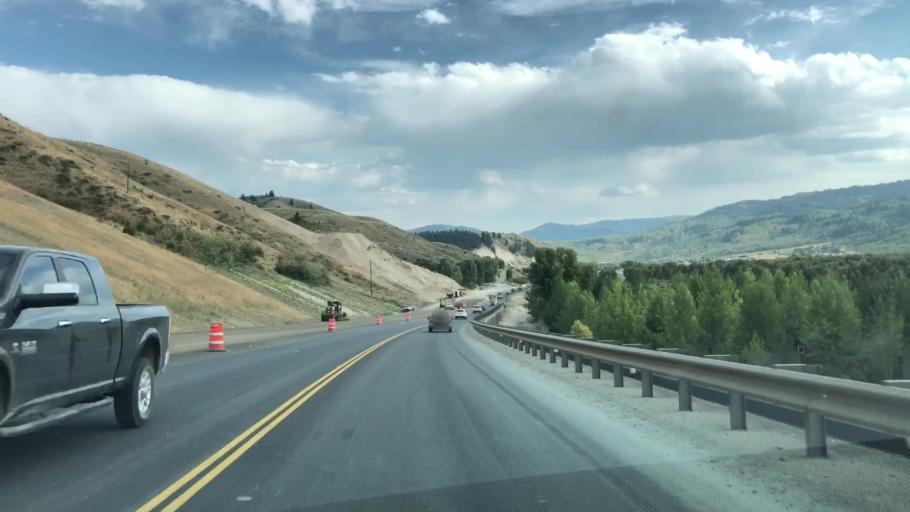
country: US
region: Wyoming
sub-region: Teton County
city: South Park
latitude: 43.3981
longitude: -110.7504
